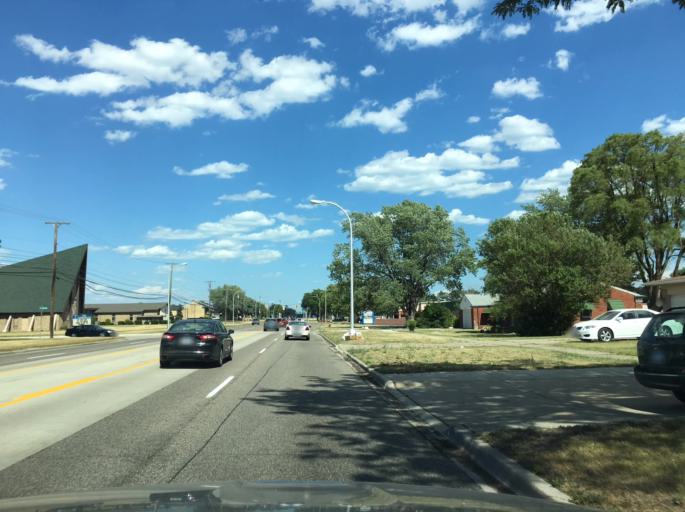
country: US
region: Michigan
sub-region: Macomb County
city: Fraser
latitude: 42.5080
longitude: -82.9807
